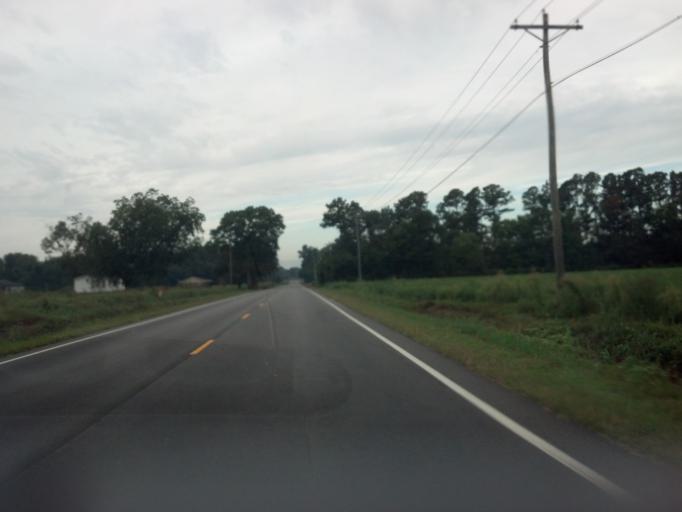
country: US
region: North Carolina
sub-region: Greene County
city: Maury
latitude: 35.4696
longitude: -77.5297
